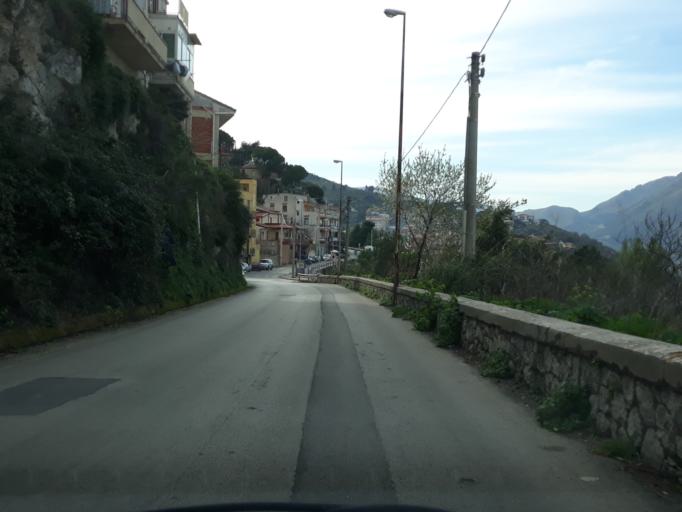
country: IT
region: Sicily
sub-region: Palermo
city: Altofonte
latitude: 38.0413
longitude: 13.2972
